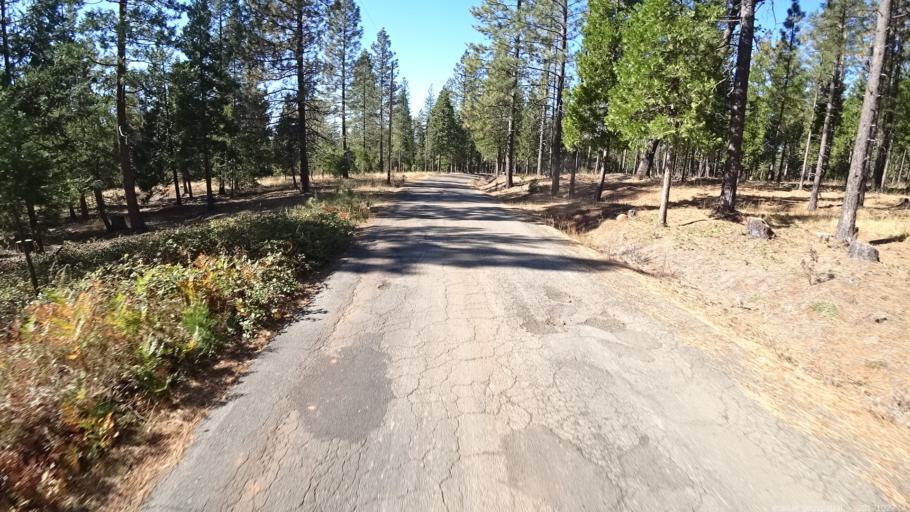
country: US
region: California
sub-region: Shasta County
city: Shingletown
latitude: 40.6150
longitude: -121.8365
